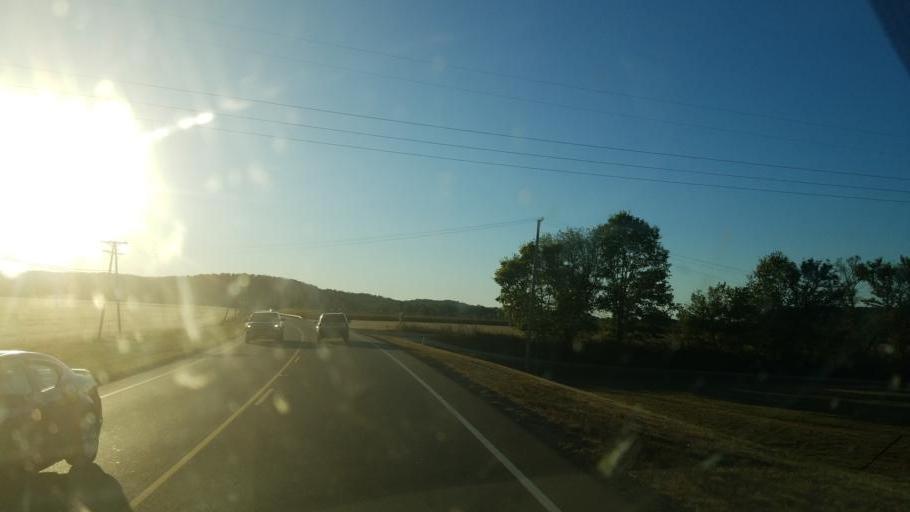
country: US
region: Ohio
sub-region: Coshocton County
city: Coshocton
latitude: 40.3025
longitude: -81.8988
